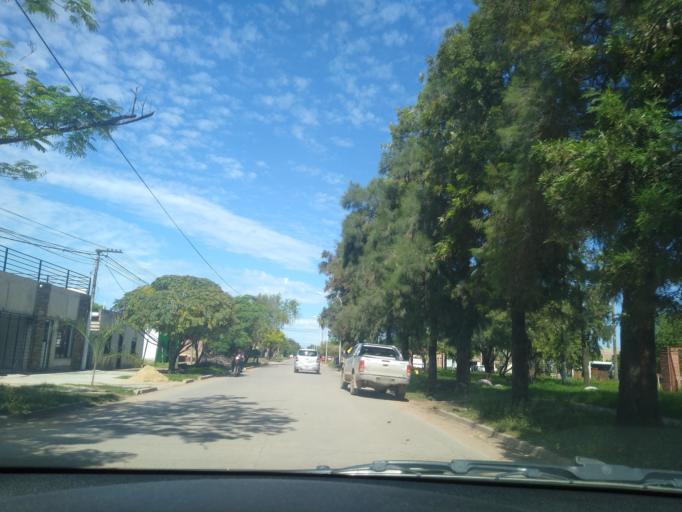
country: AR
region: Chaco
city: Presidencia Roque Saenz Pena
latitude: -26.7774
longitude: -60.4253
